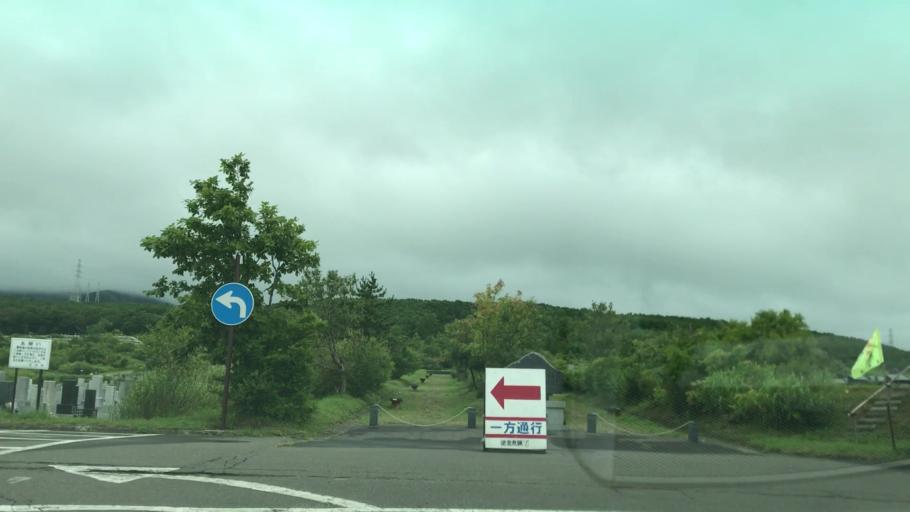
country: JP
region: Hokkaido
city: Muroran
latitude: 42.3926
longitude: 141.0003
